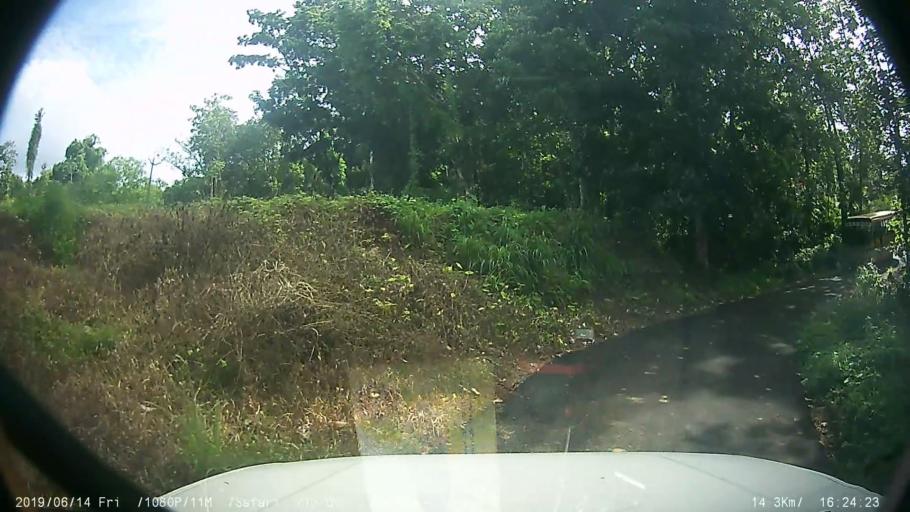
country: IN
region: Kerala
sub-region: Kottayam
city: Palackattumala
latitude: 9.7749
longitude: 76.5985
